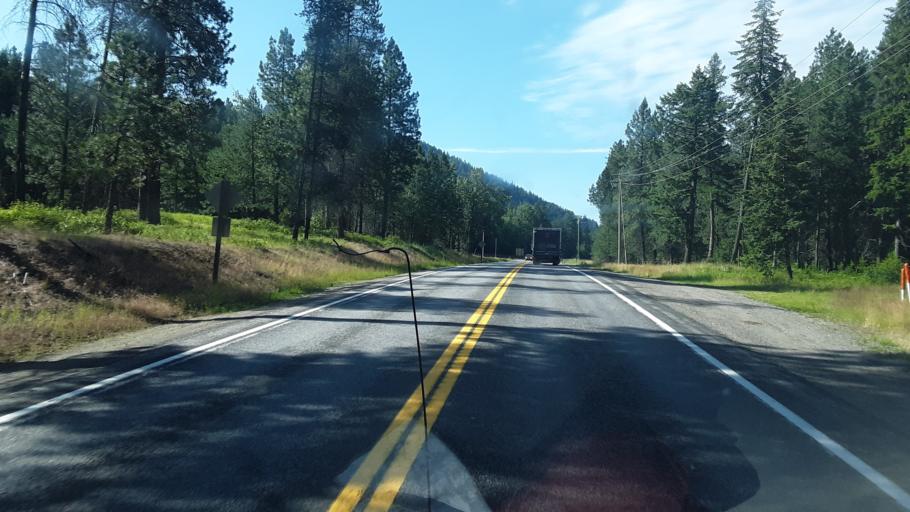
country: US
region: Idaho
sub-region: Boundary County
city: Bonners Ferry
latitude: 48.5160
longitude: -116.4436
